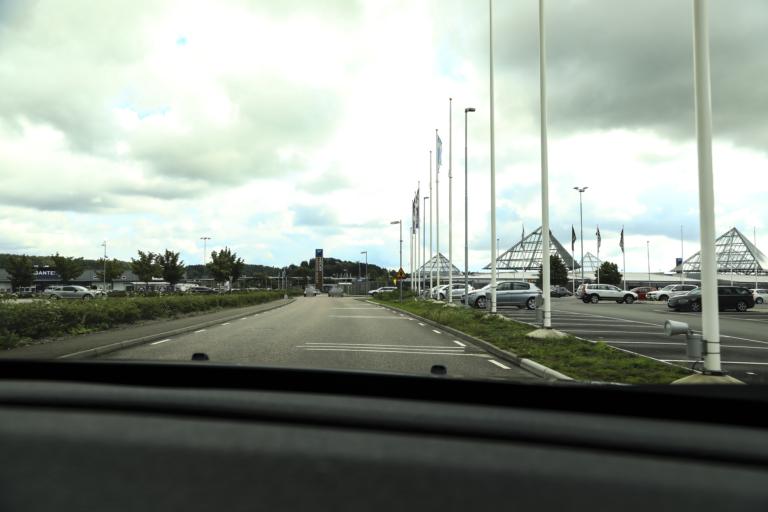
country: SE
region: Halland
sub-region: Kungsbacka Kommun
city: Kungsbacka
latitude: 57.5151
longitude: 12.0739
